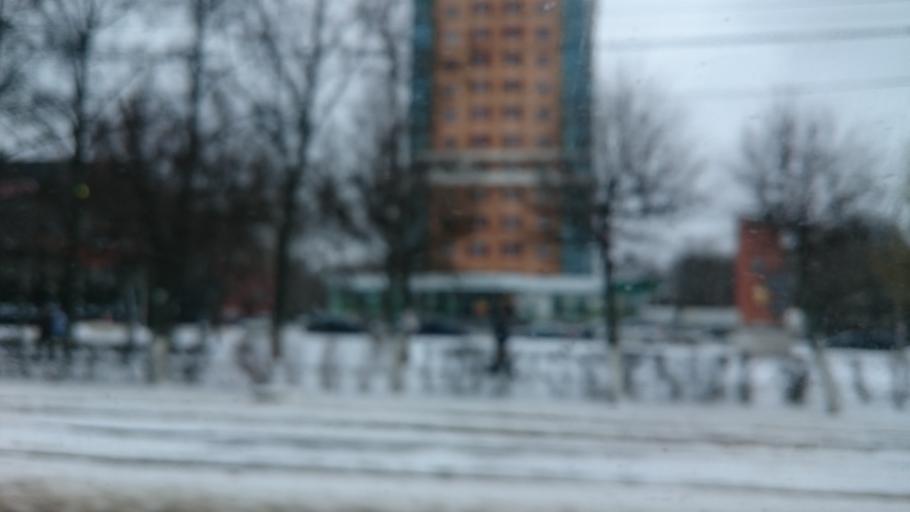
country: RU
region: Tula
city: Mendeleyevskiy
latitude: 54.1622
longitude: 37.5867
